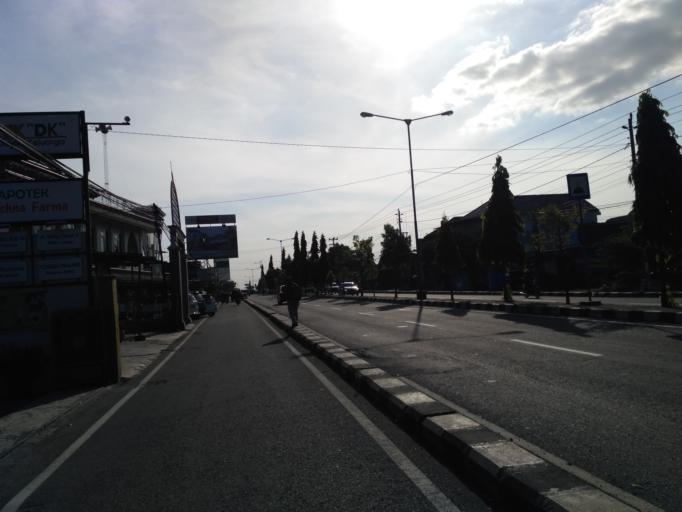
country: ID
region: Daerah Istimewa Yogyakarta
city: Depok
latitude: -7.7653
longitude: 110.4270
